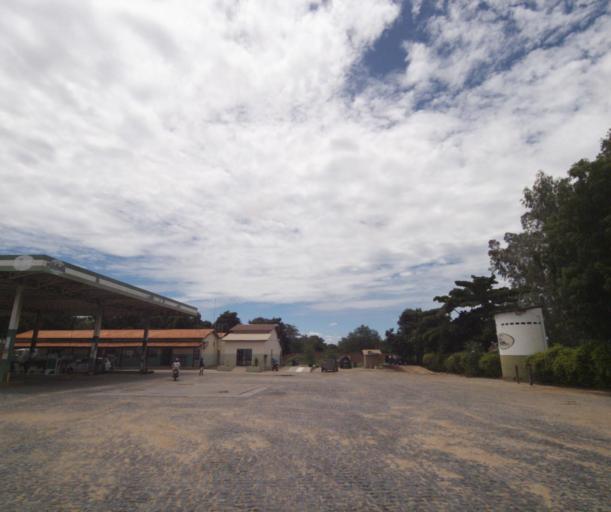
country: BR
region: Bahia
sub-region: Carinhanha
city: Carinhanha
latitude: -14.3270
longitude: -43.7627
